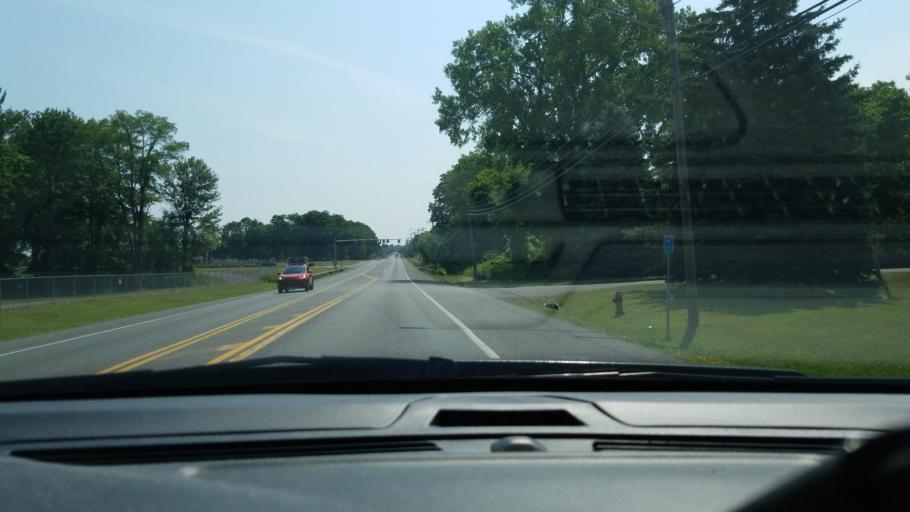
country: US
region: New York
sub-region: Onondaga County
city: Lyncourt
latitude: 43.0989
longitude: -76.1056
